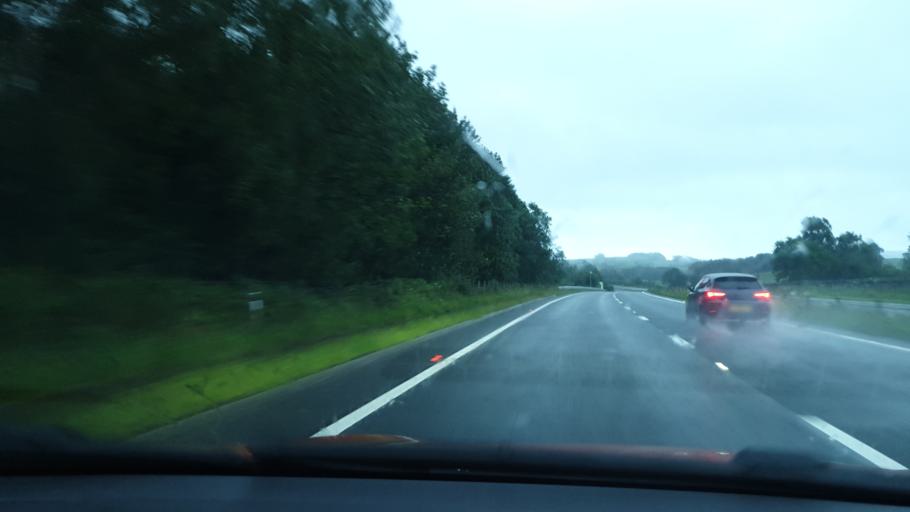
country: GB
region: England
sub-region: Cumbria
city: Grange-over-Sands
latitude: 54.2533
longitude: -2.9420
